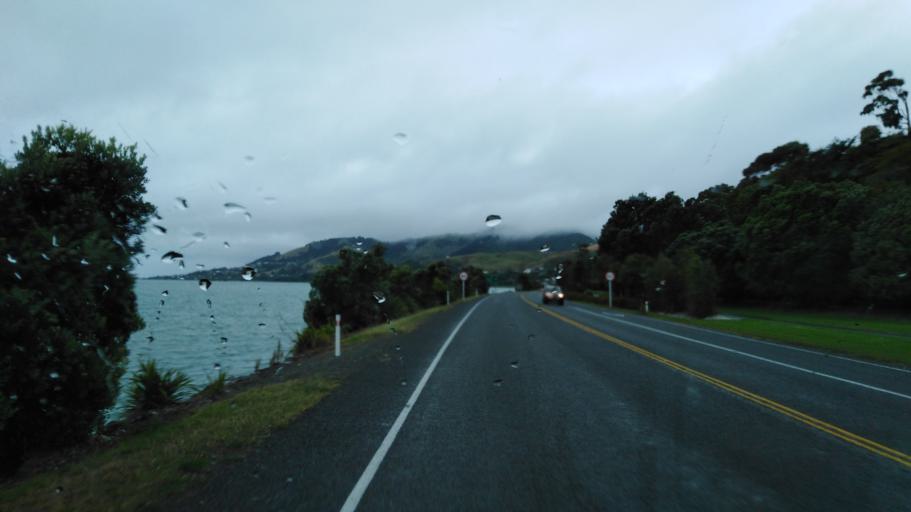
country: NZ
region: Nelson
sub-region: Nelson City
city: Nelson
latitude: -41.2556
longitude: 173.2997
